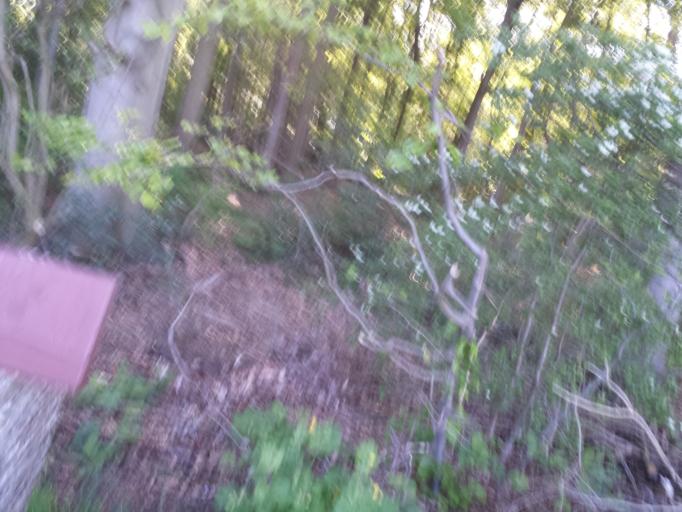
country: DE
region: Lower Saxony
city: Lilienthal
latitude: 53.1435
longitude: 8.9138
